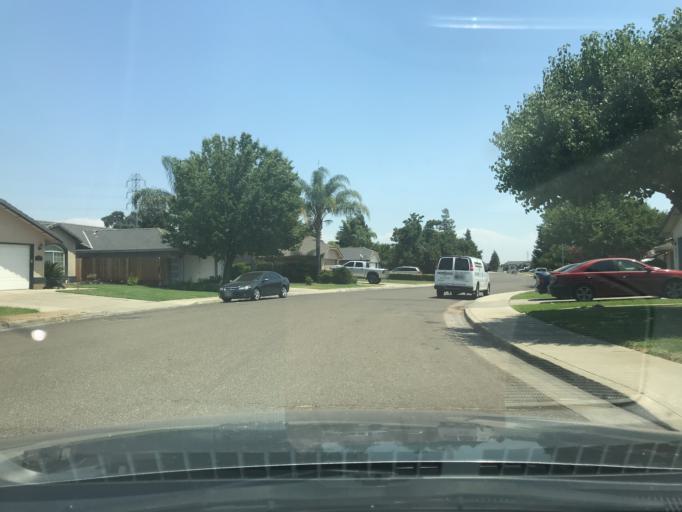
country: US
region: California
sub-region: Merced County
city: Atwater
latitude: 37.3668
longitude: -120.5944
